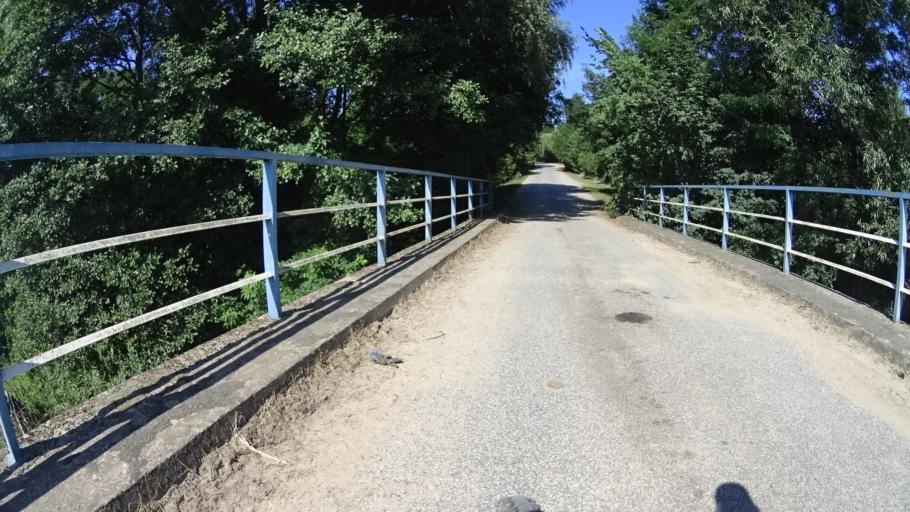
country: PL
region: Masovian Voivodeship
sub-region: Powiat bialobrzeski
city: Bialobrzegi
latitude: 51.6655
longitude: 20.9176
